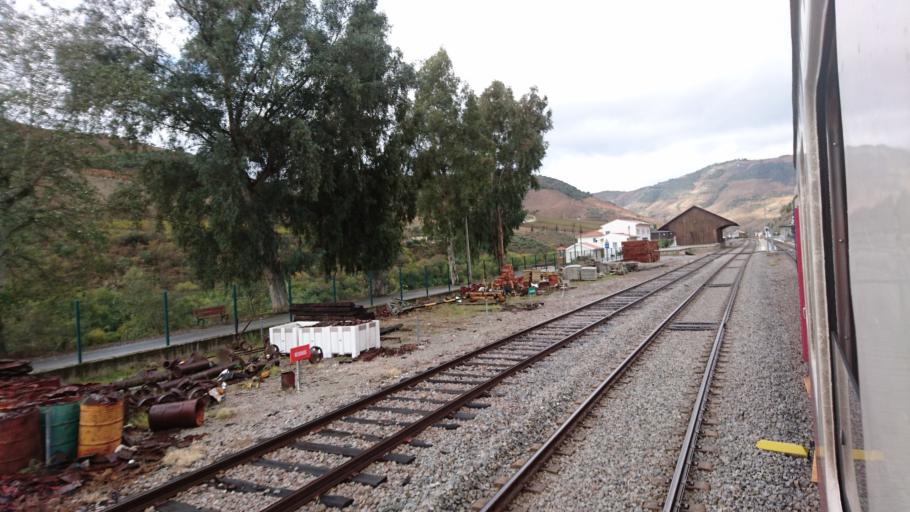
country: PT
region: Viseu
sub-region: Sao Joao da Pesqueira
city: Sao Joao da Pesqueira
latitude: 41.2067
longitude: -7.4178
